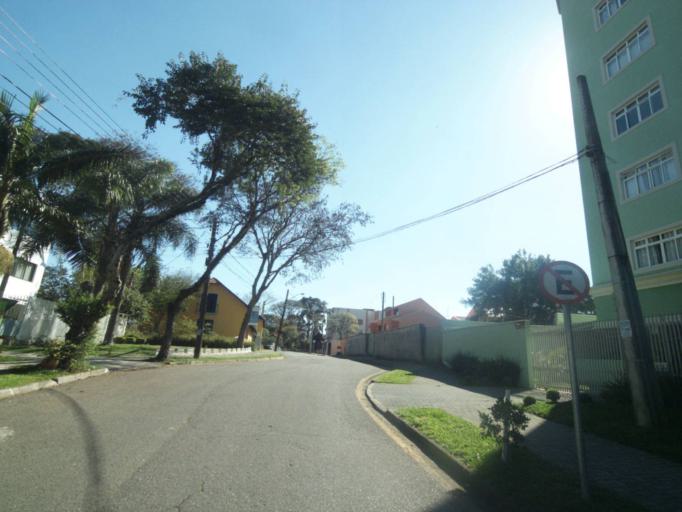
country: BR
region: Parana
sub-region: Curitiba
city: Curitiba
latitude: -25.3939
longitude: -49.2326
